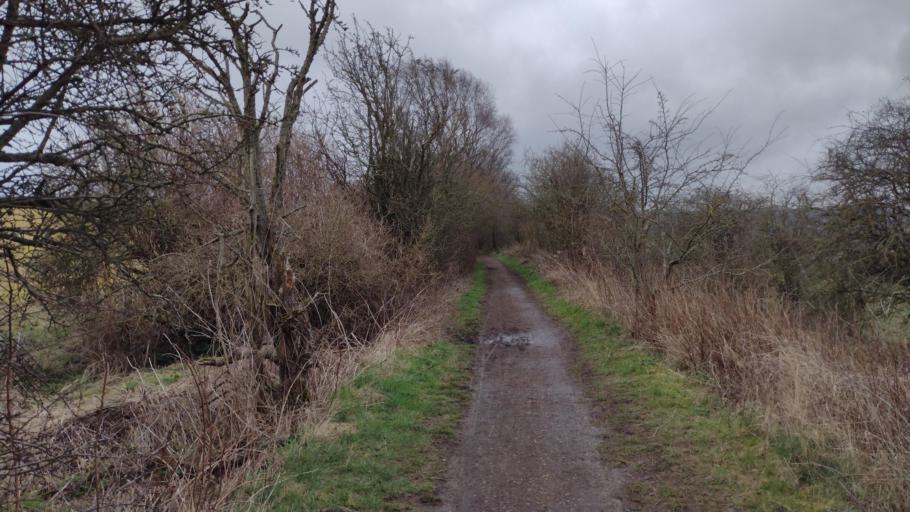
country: GB
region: England
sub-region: Wiltshire
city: Marlborough
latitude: 51.4333
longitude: -1.7265
